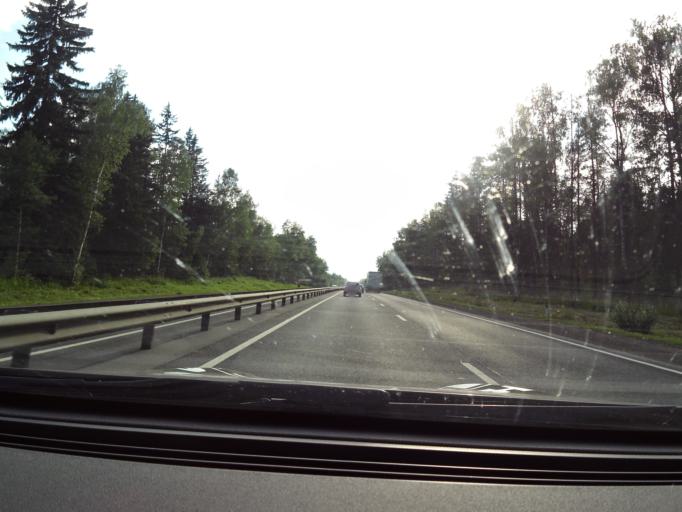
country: RU
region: Vladimir
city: Novki
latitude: 56.2012
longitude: 41.0865
